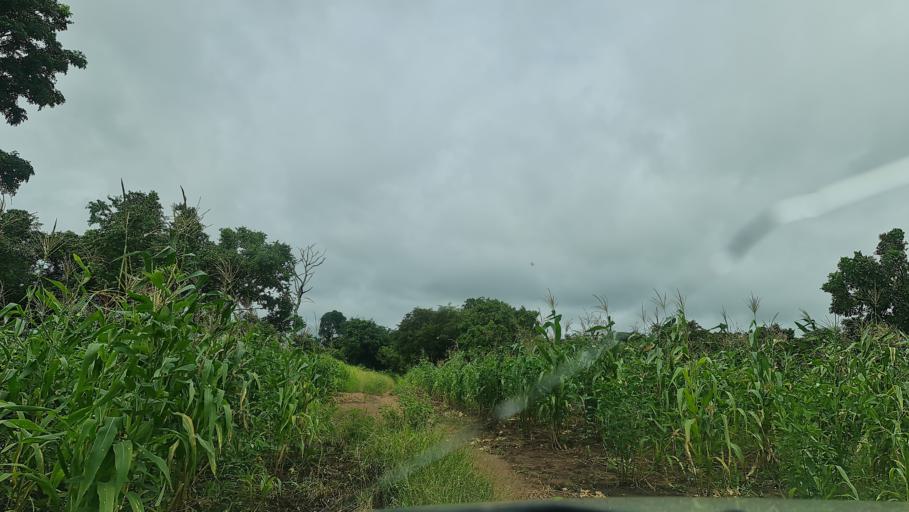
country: MW
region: Southern Region
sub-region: Nsanje District
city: Nsanje
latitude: -17.3807
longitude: 35.7766
